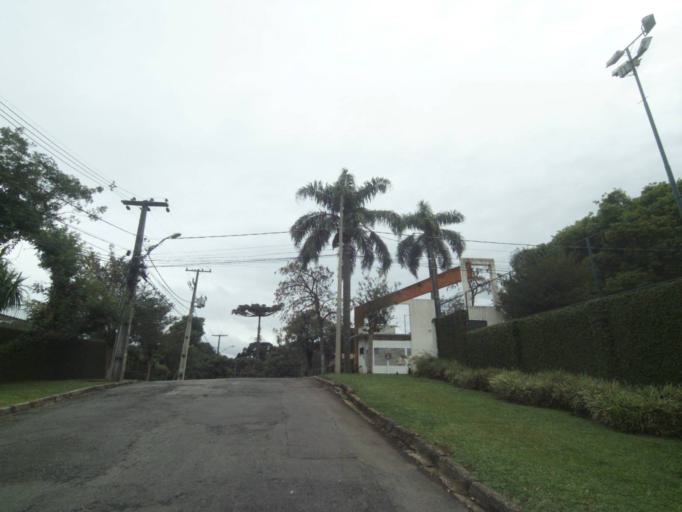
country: BR
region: Parana
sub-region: Curitiba
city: Curitiba
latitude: -25.4523
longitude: -49.3307
